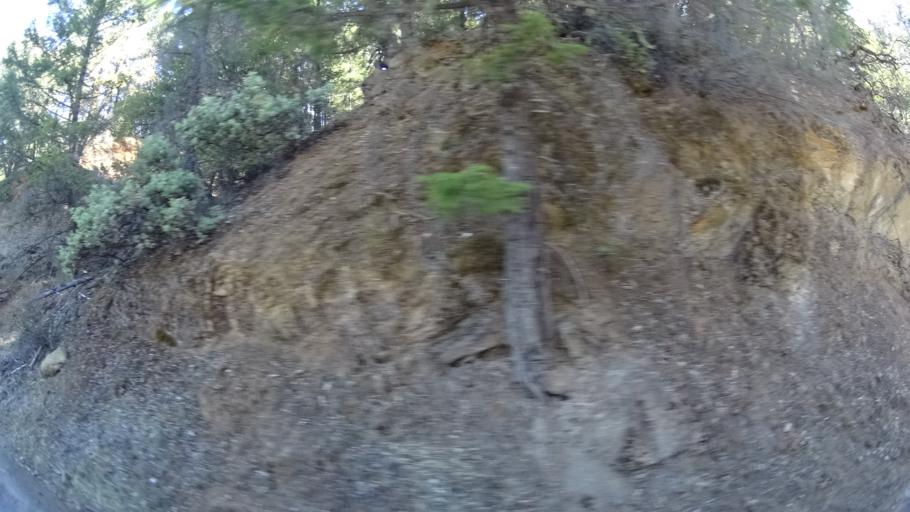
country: US
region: California
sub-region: Humboldt County
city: Willow Creek
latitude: 41.1939
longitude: -123.2158
